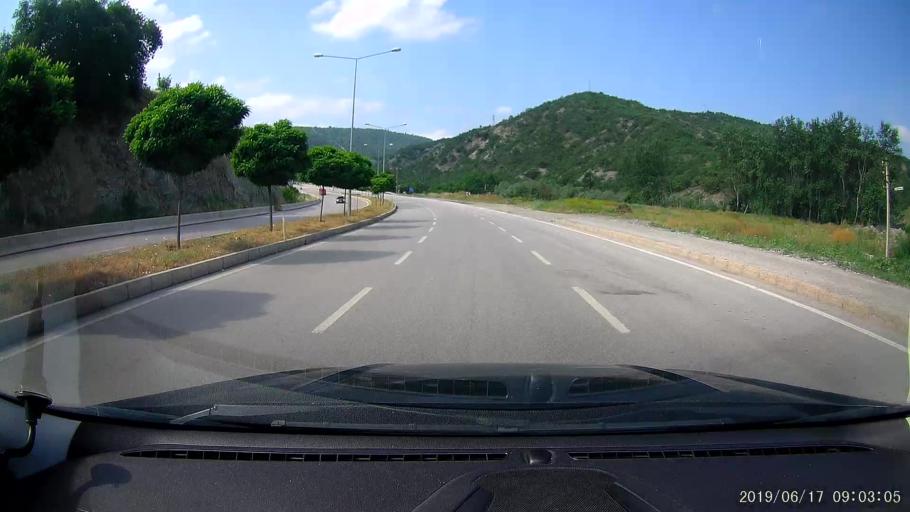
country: TR
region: Amasya
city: Tasova
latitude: 40.7596
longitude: 36.3027
